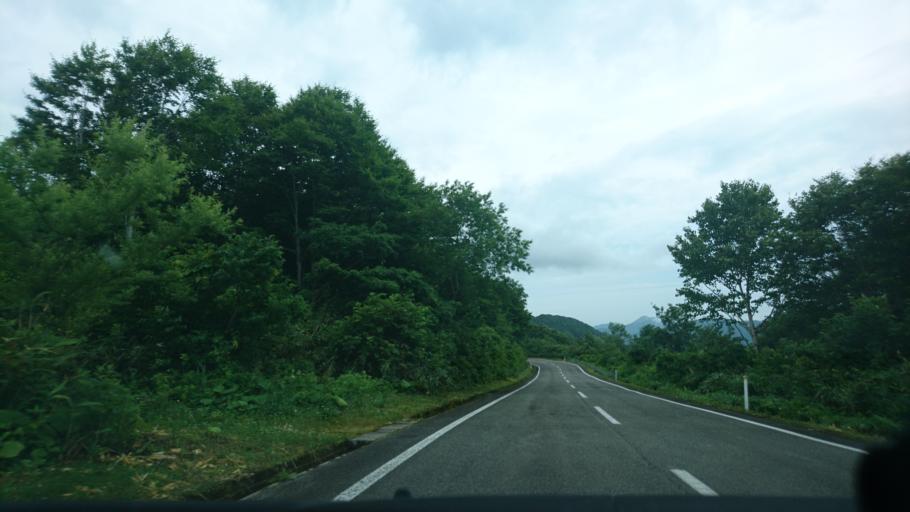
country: JP
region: Akita
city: Yuzawa
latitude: 39.1544
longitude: 140.7543
